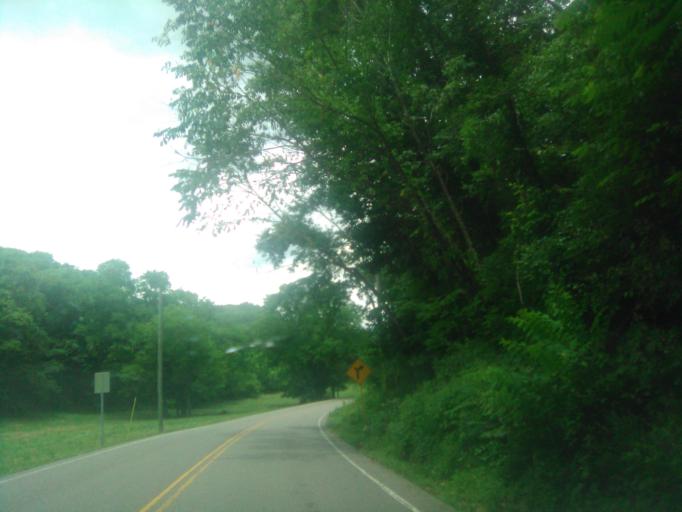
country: US
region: Tennessee
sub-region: Davidson County
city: Forest Hills
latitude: 36.0693
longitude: -86.8721
